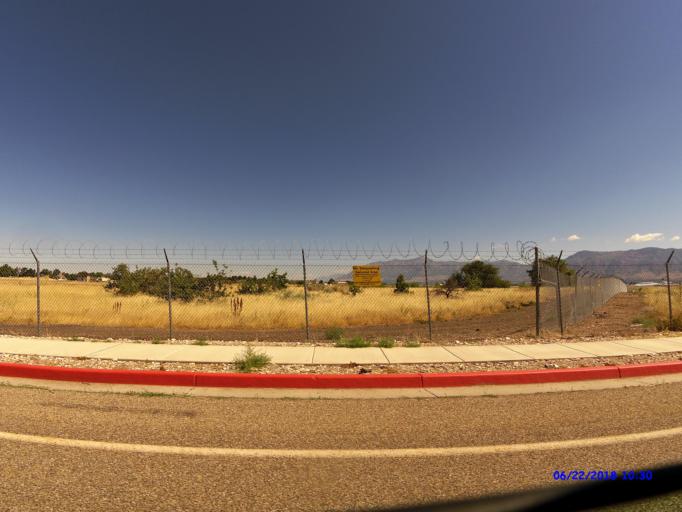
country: US
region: Utah
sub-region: Weber County
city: Riverdale
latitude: 41.1835
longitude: -112.0227
